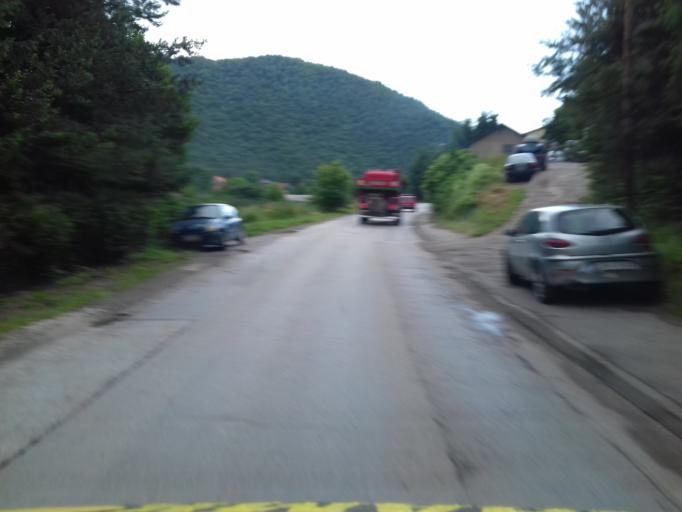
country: BA
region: Federation of Bosnia and Herzegovina
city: Visoko
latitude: 43.9736
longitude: 18.1882
